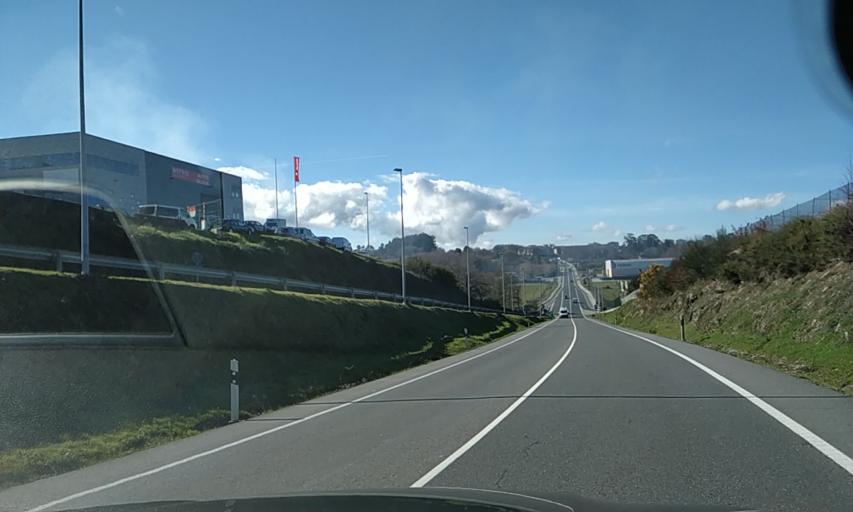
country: ES
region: Galicia
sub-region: Provincia de Pontevedra
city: Silleda
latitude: 42.6937
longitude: -8.2273
